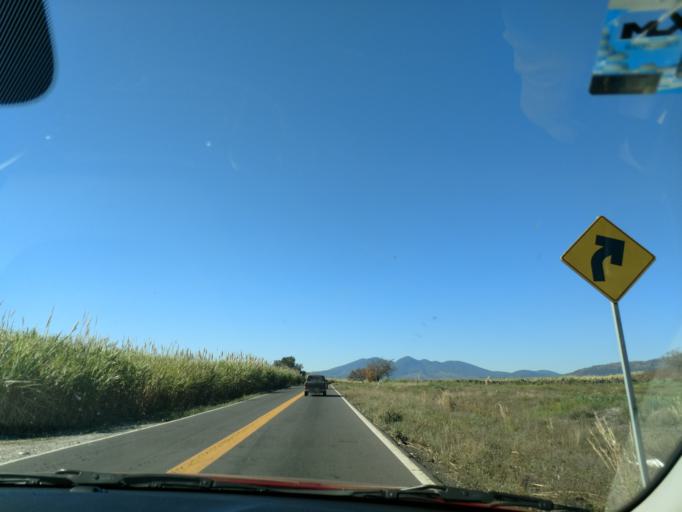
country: MX
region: Nayarit
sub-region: Ahuacatlan
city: Ahuacatlan
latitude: 21.1316
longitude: -104.6044
